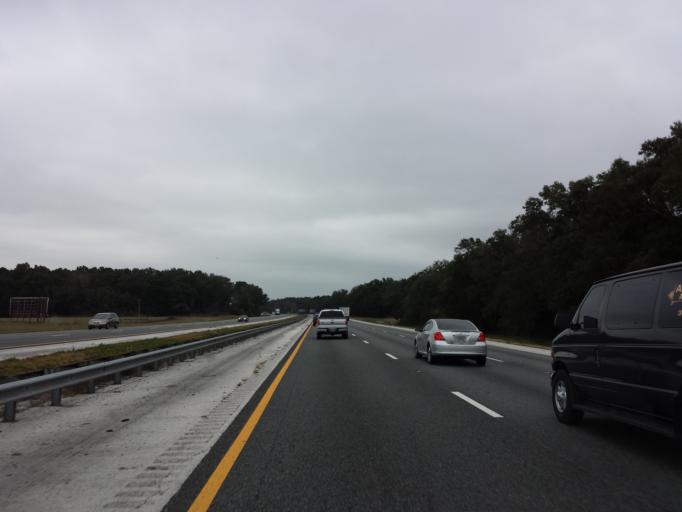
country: US
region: Florida
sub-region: Marion County
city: Ocala
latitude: 29.2530
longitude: -82.1898
